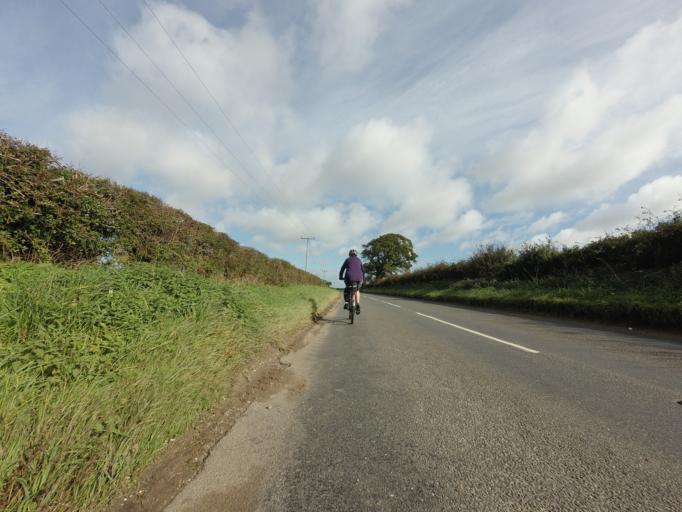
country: GB
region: England
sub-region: Norfolk
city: Wells-next-the-Sea
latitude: 52.9039
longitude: 0.6900
